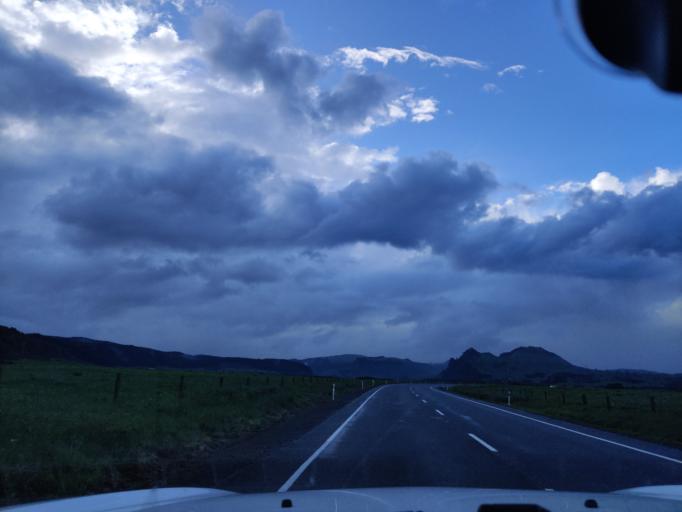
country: NZ
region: Waikato
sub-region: South Waikato District
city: Tokoroa
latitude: -38.3986
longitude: 175.7879
